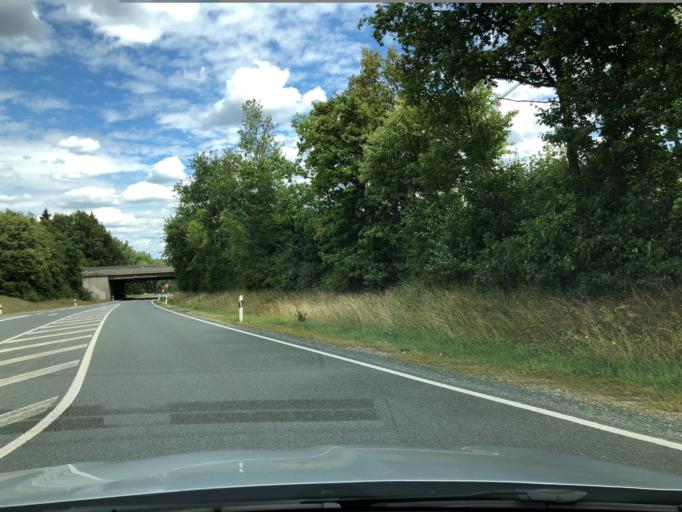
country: DE
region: Bavaria
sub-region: Upper Palatinate
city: Illschwang
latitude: 49.4276
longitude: 11.6533
